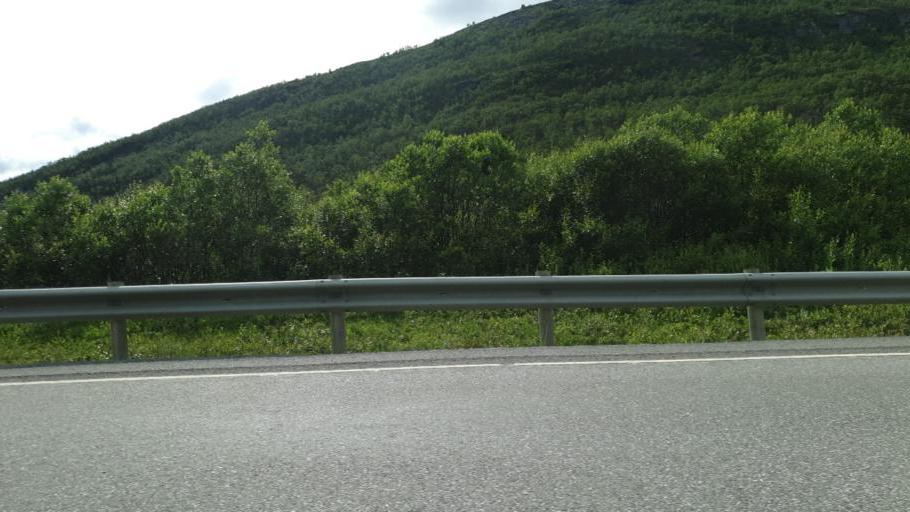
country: NO
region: Sor-Trondelag
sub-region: Oppdal
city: Oppdal
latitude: 62.3211
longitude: 9.6209
